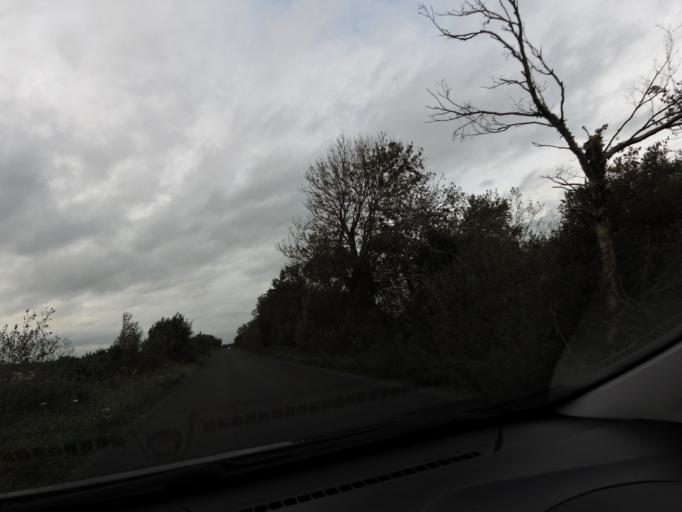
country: IE
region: Leinster
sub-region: Uibh Fhaili
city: Ferbane
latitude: 53.2387
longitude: -7.8268
